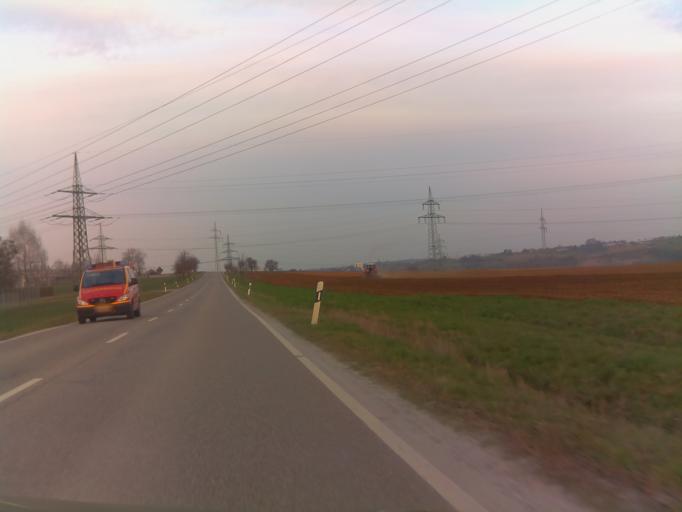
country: DE
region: Baden-Wuerttemberg
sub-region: Regierungsbezirk Stuttgart
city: Oberriexingen
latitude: 48.9013
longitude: 9.0430
